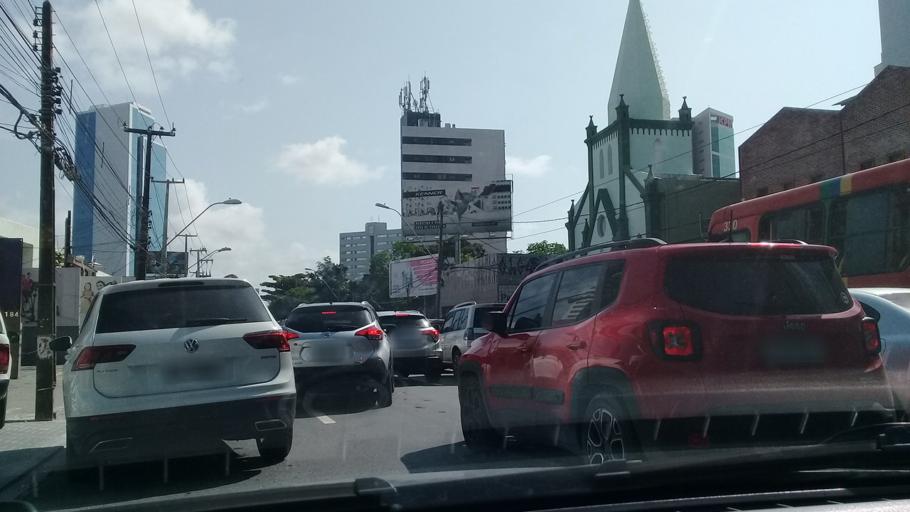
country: BR
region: Pernambuco
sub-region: Recife
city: Recife
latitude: -8.0923
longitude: -34.8838
